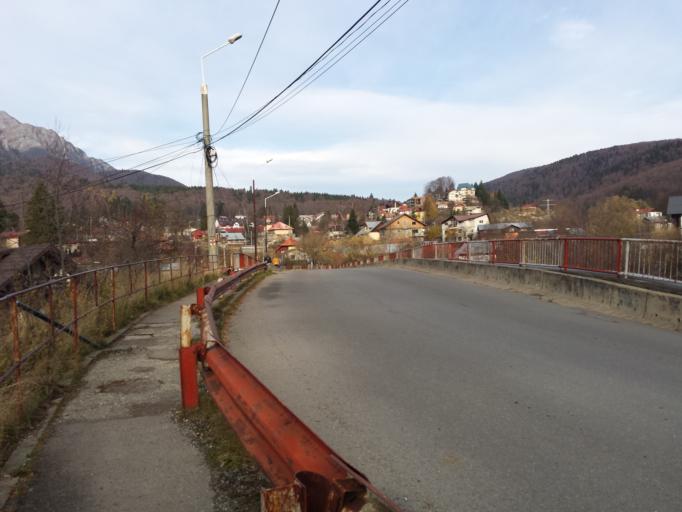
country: RO
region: Prahova
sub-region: Oras Busteni
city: Busteni
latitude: 45.4150
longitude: 25.5409
